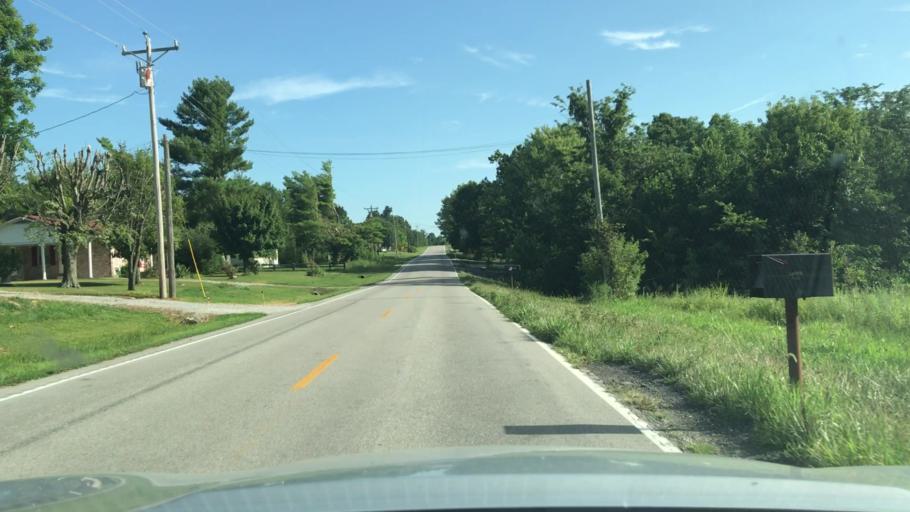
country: US
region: Kentucky
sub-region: Todd County
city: Elkton
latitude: 36.9248
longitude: -87.1625
